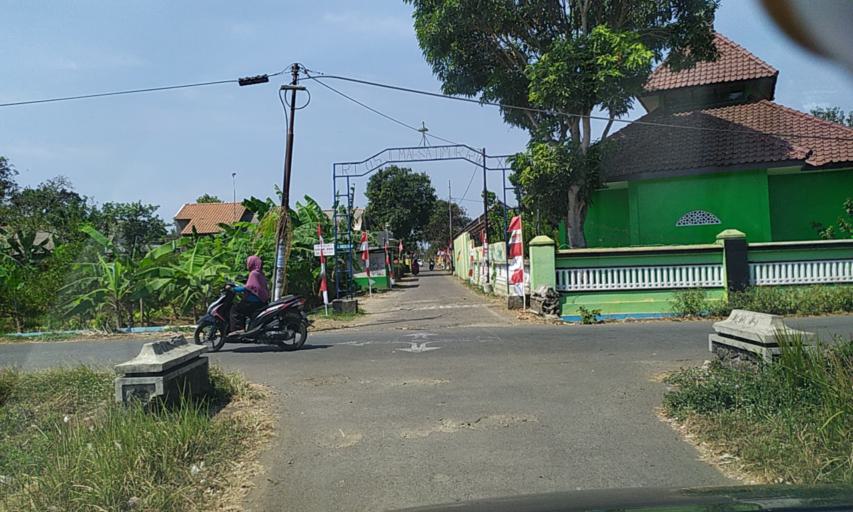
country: ID
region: Central Java
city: Rejanegara
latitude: -7.6732
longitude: 109.0595
